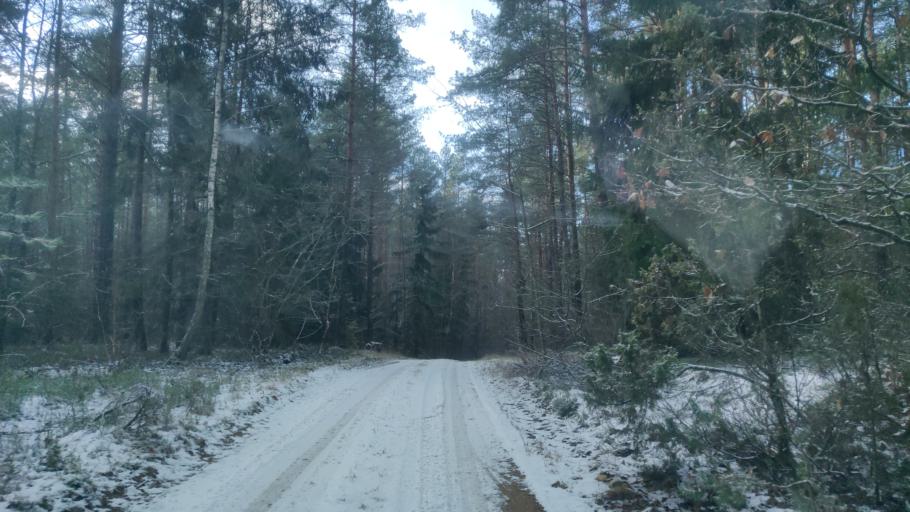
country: LT
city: Trakai
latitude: 54.5645
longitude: 24.9176
